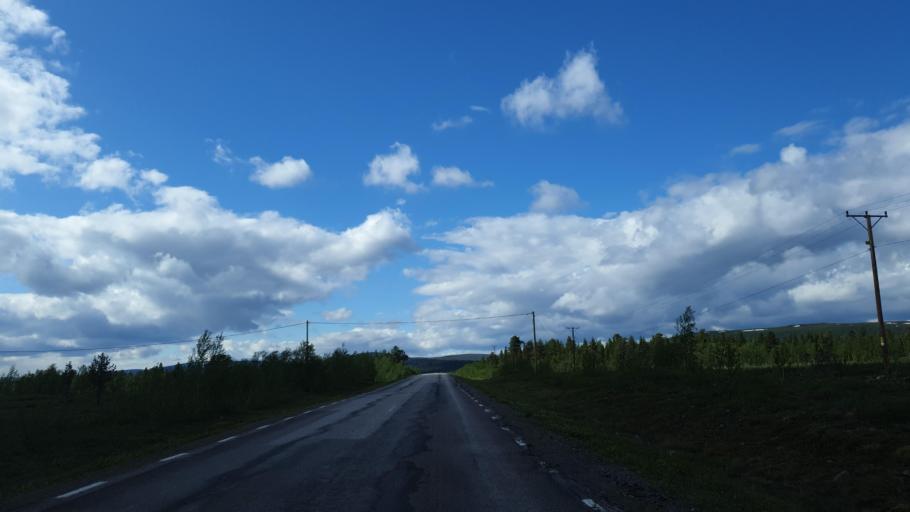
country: SE
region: Norrbotten
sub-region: Kiruna Kommun
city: Kiruna
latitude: 67.7731
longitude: 19.9730
